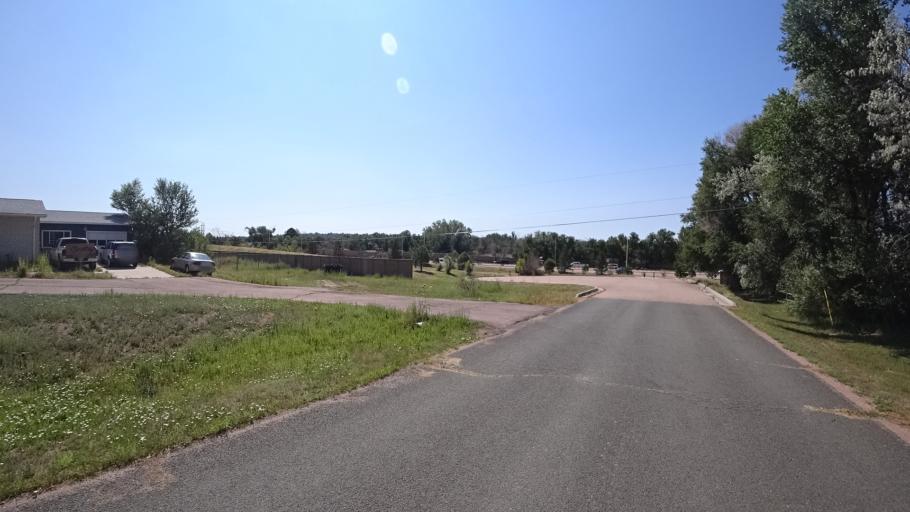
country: US
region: Colorado
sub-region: El Paso County
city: Air Force Academy
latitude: 38.9338
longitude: -104.7876
